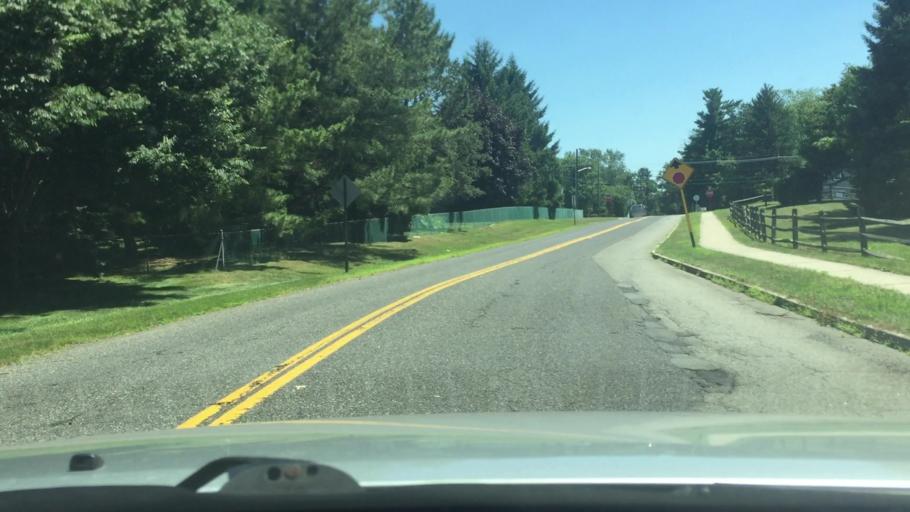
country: US
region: New Jersey
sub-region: Middlesex County
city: East Brunswick
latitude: 40.4199
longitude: -74.3997
